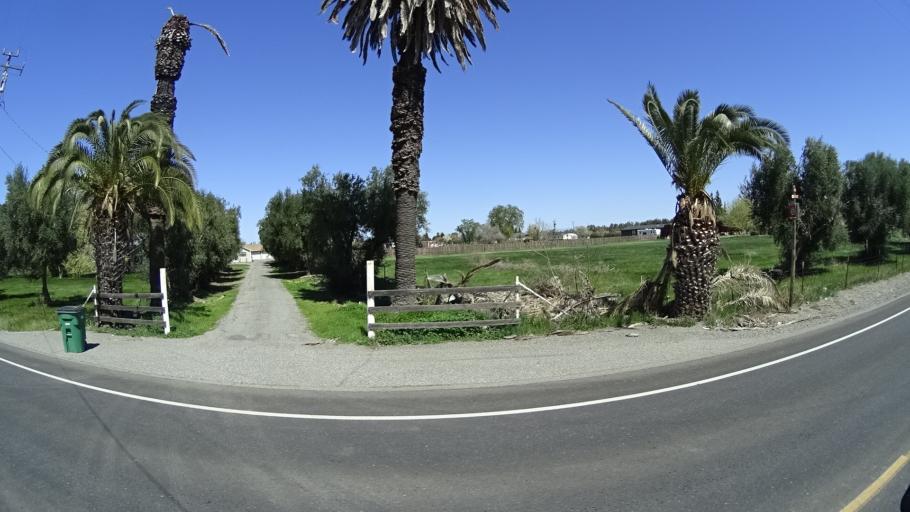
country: US
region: California
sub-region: Glenn County
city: Orland
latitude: 39.7612
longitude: -122.2318
